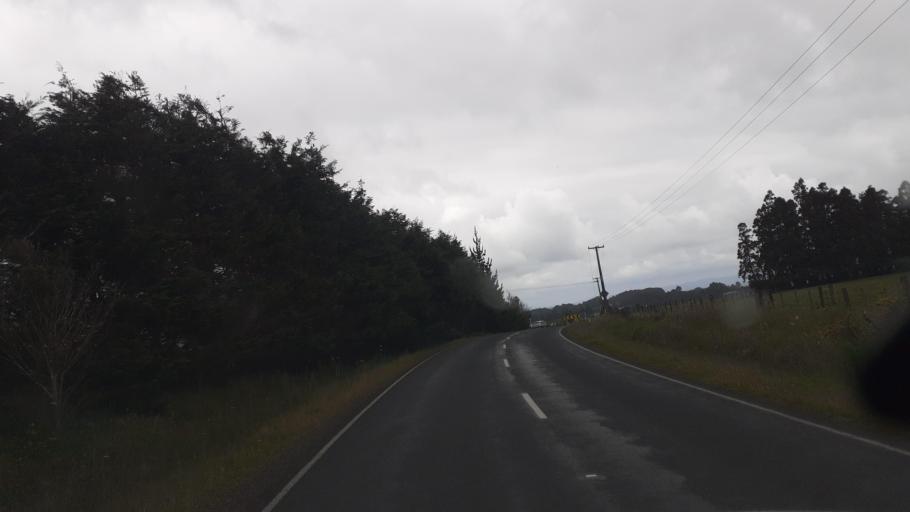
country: NZ
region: Northland
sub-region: Far North District
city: Waimate North
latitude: -35.2788
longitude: 173.8309
